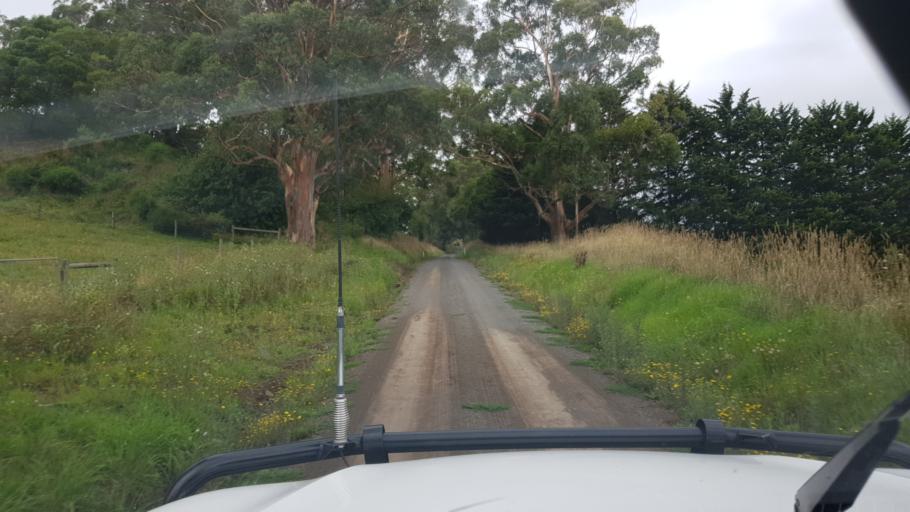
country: AU
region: Victoria
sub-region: Baw Baw
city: Warragul
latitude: -38.0404
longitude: 145.9101
